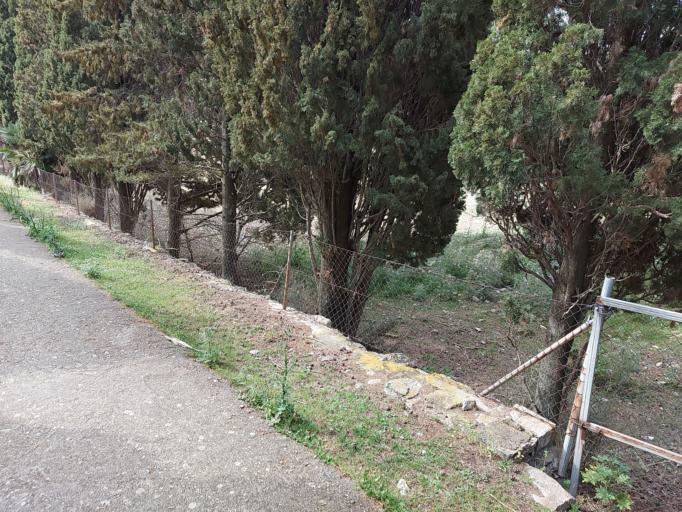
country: ES
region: Balearic Islands
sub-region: Illes Balears
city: Arta
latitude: 39.7369
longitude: 3.3115
